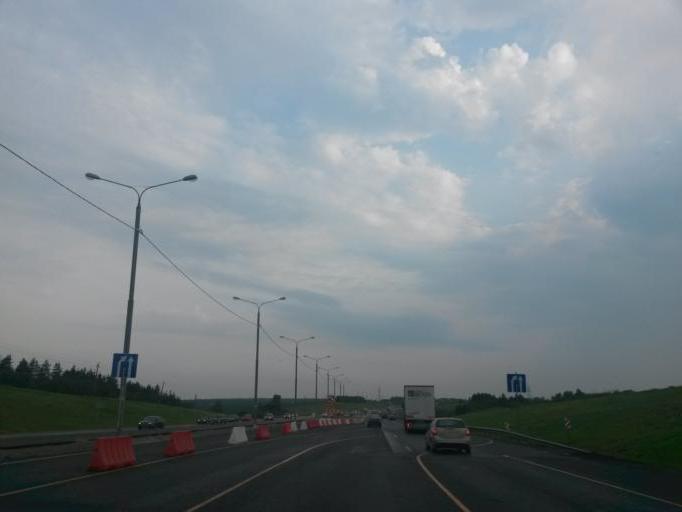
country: RU
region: Moskovskaya
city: Klimovsk
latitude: 55.3508
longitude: 37.5922
